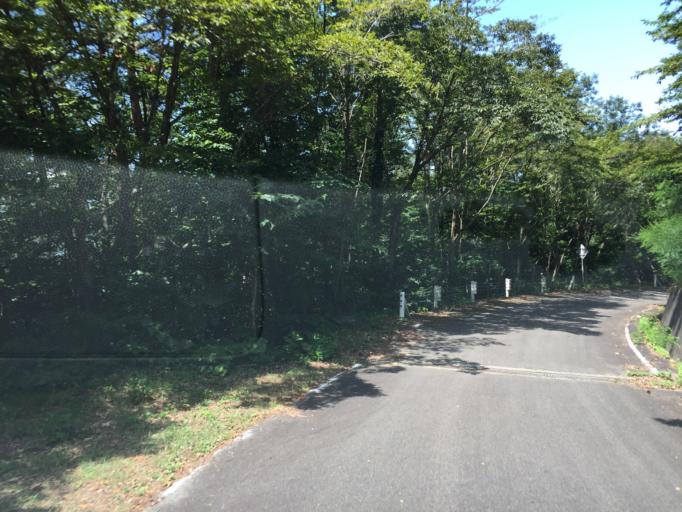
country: JP
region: Fukushima
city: Inawashiro
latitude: 37.4407
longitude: 140.0588
